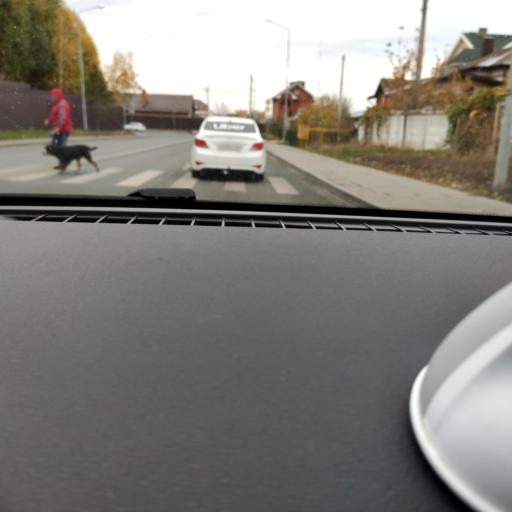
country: RU
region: Samara
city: Samara
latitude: 53.2701
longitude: 50.2181
